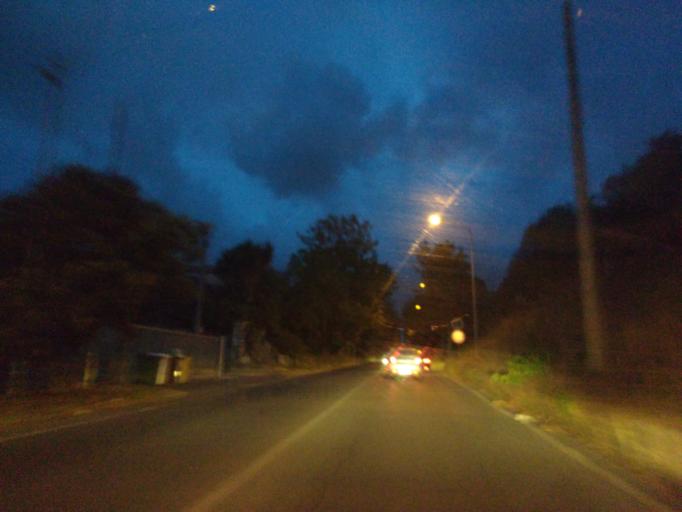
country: IT
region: Latium
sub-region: Citta metropolitana di Roma Capitale
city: Anzio
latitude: 41.4574
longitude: 12.6210
